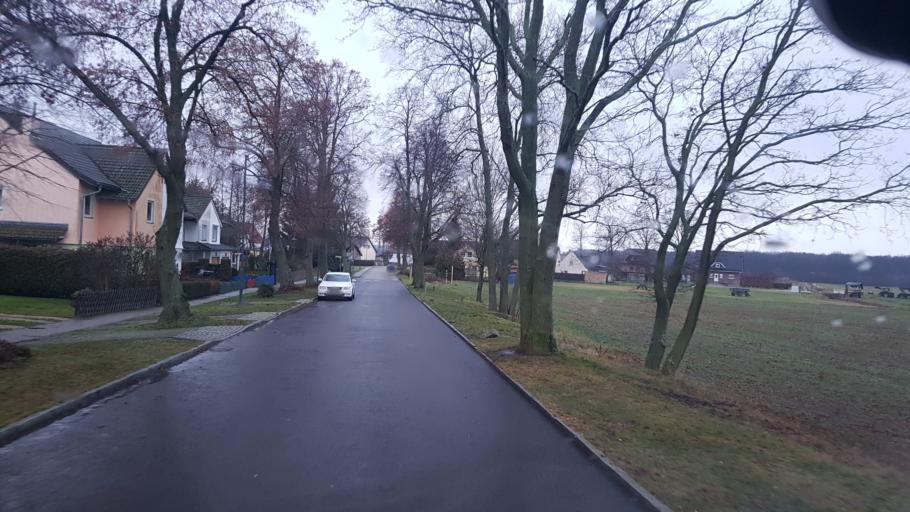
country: DE
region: Brandenburg
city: Ludwigsfelde
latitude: 52.3183
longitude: 13.1938
